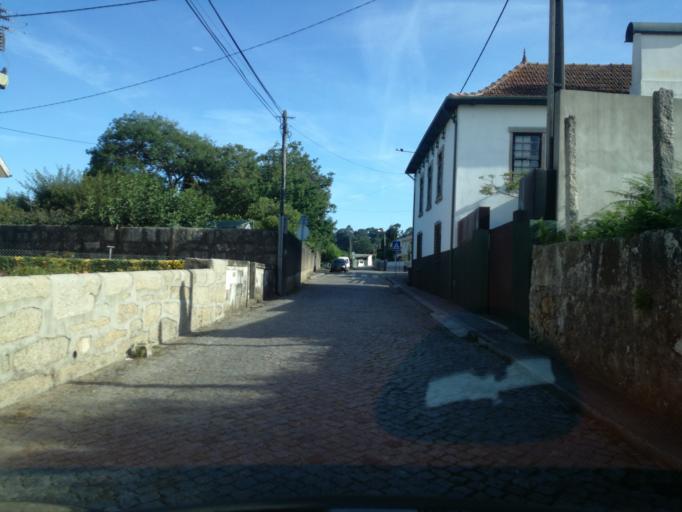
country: PT
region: Porto
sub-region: Maia
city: Nogueira
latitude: 41.2558
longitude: -8.5914
